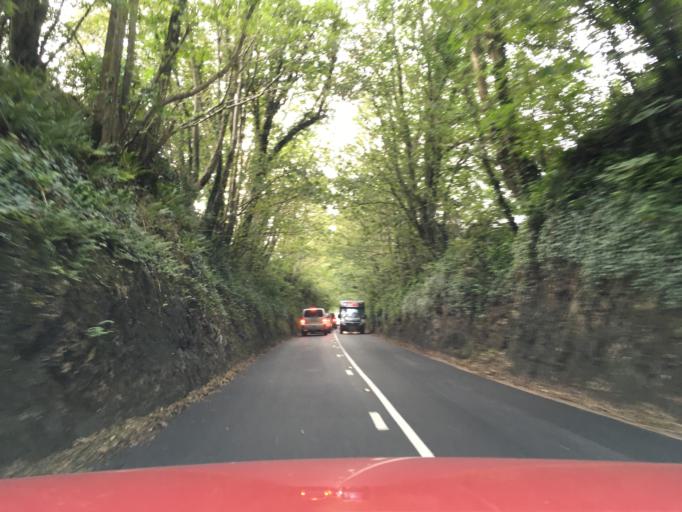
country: GB
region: England
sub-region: Devon
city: Modbury
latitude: 50.3501
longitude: -3.9052
